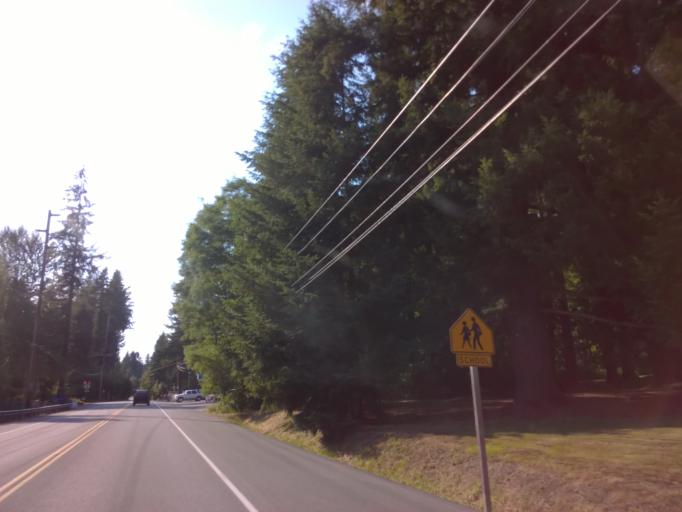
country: US
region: Washington
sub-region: King County
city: Cottage Lake
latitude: 47.7581
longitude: -122.0877
